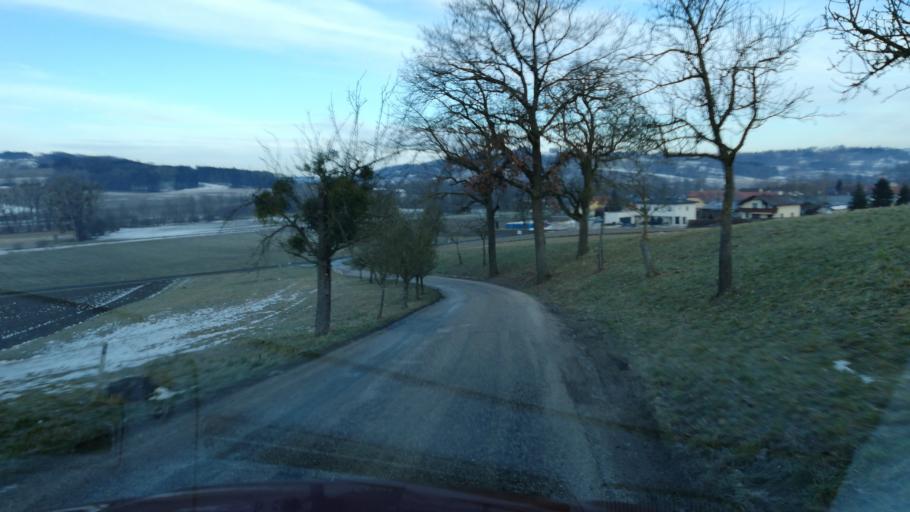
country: AT
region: Upper Austria
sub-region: Wels-Land
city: Buchkirchen
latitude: 48.2448
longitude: 13.9797
